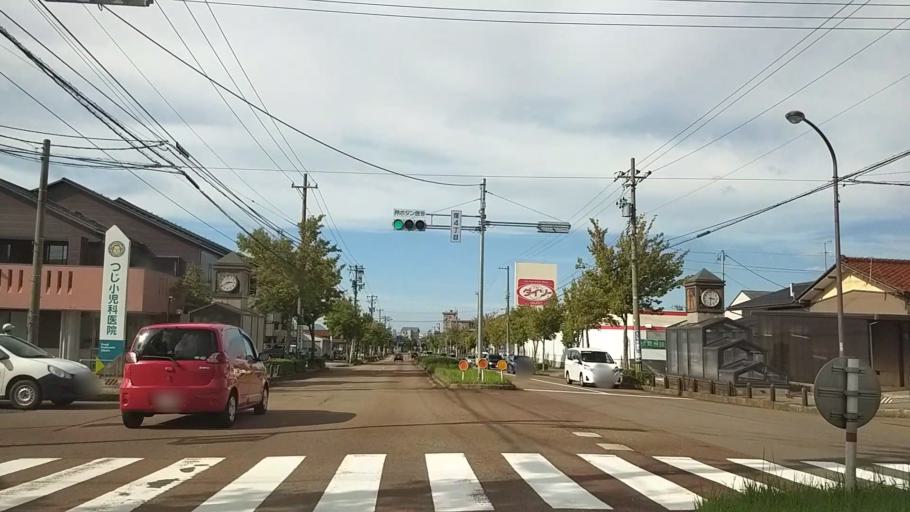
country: JP
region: Ishikawa
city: Nonoichi
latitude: 36.5257
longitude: 136.6389
